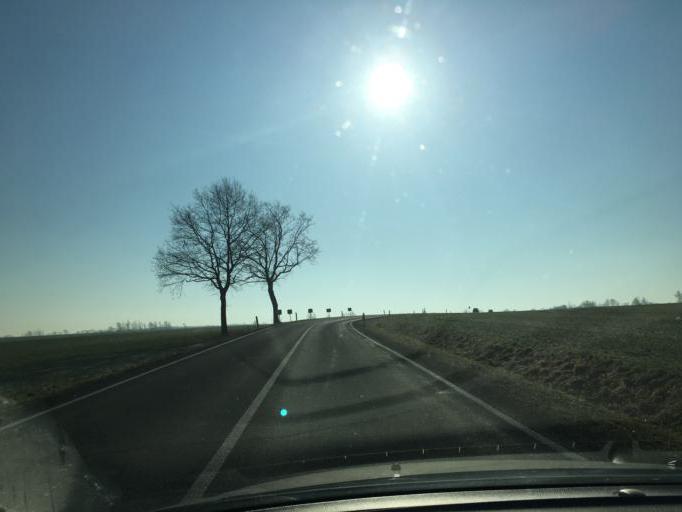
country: DE
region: Saxony
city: Otterwisch
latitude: 51.1867
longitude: 12.6144
